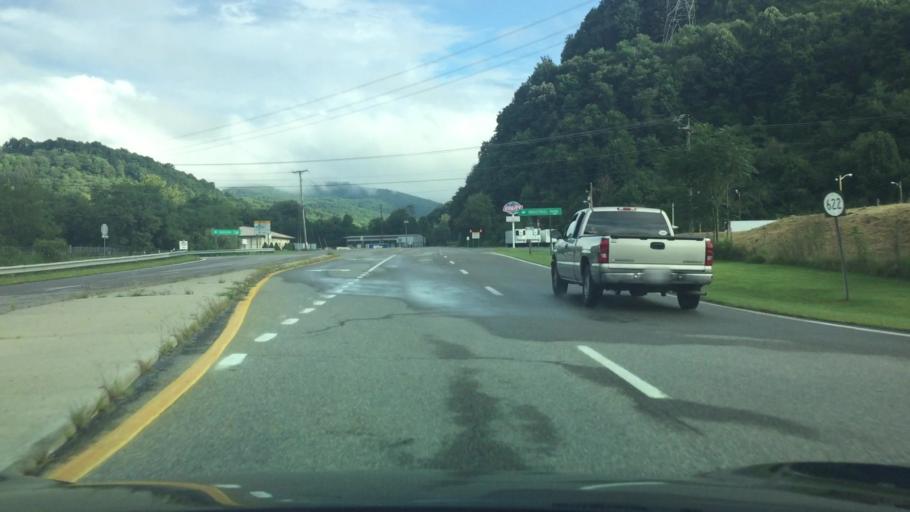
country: US
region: Virginia
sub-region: Smyth County
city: Atkins
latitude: 36.8620
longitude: -81.4337
